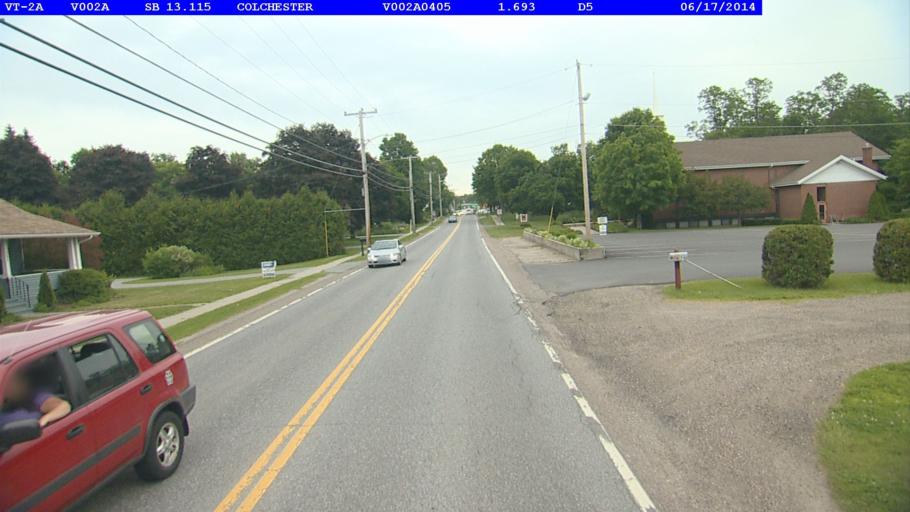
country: US
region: Vermont
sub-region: Chittenden County
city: Colchester
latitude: 44.5453
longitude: -73.1519
